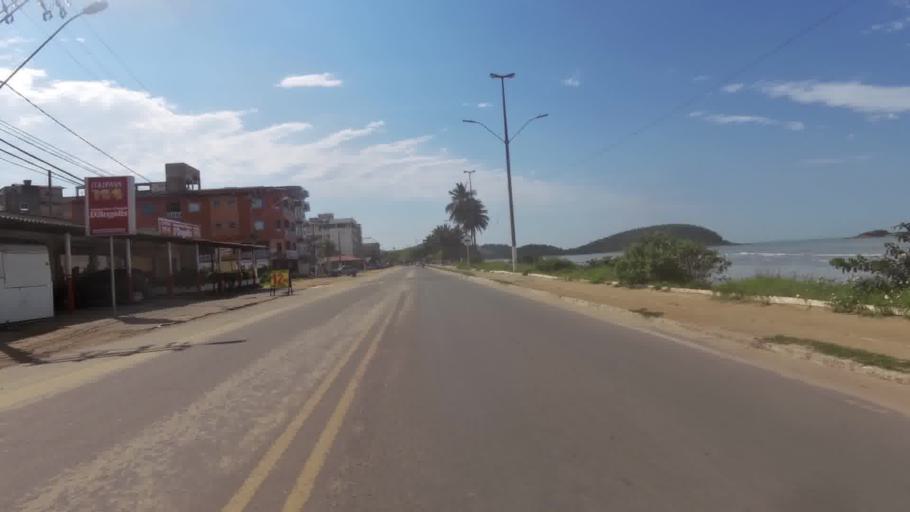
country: BR
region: Espirito Santo
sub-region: Piuma
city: Piuma
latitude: -20.8437
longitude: -40.7341
